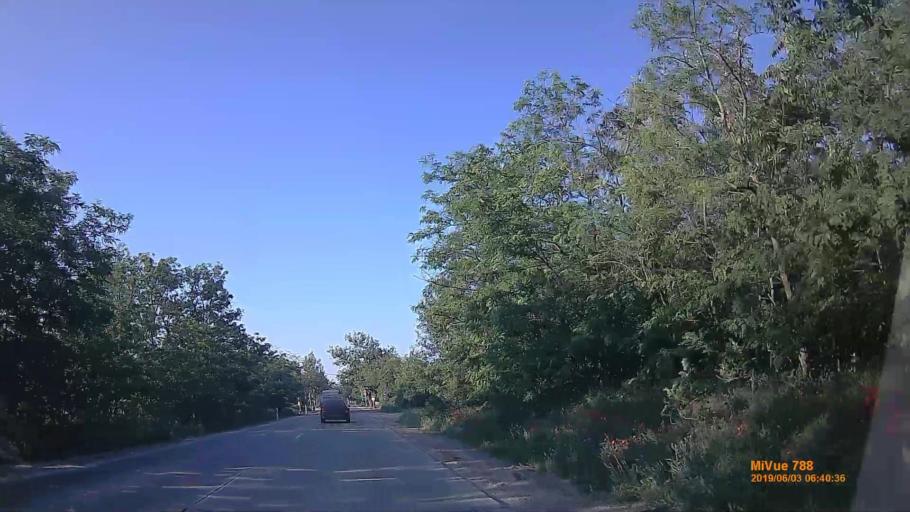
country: HU
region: Pest
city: Delegyhaza
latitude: 47.2769
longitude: 19.1062
